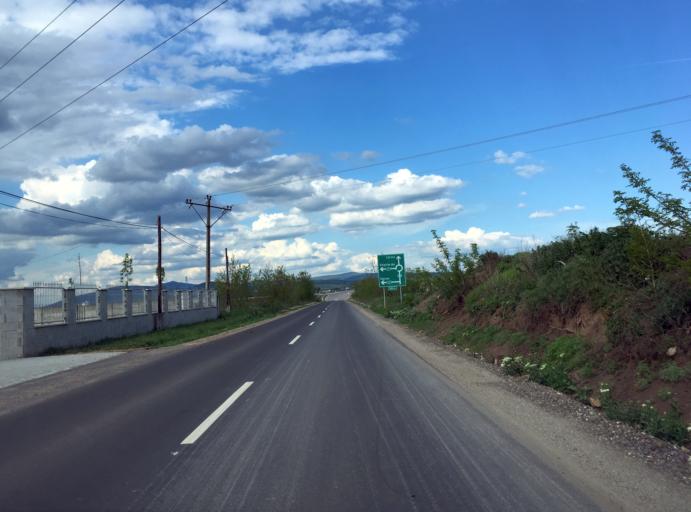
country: HU
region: Heves
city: Lorinci
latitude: 47.7279
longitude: 19.6607
